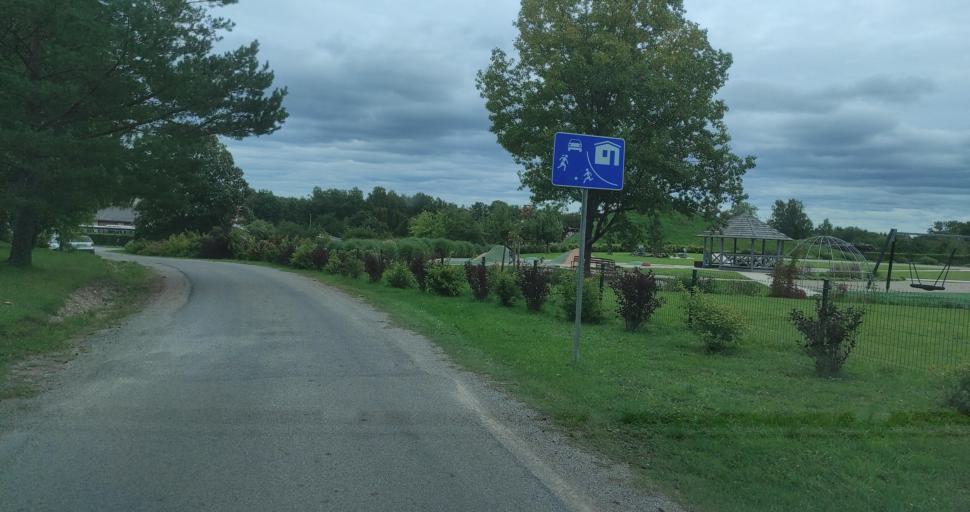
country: LV
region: Kuldigas Rajons
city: Kuldiga
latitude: 56.9168
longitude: 21.9648
